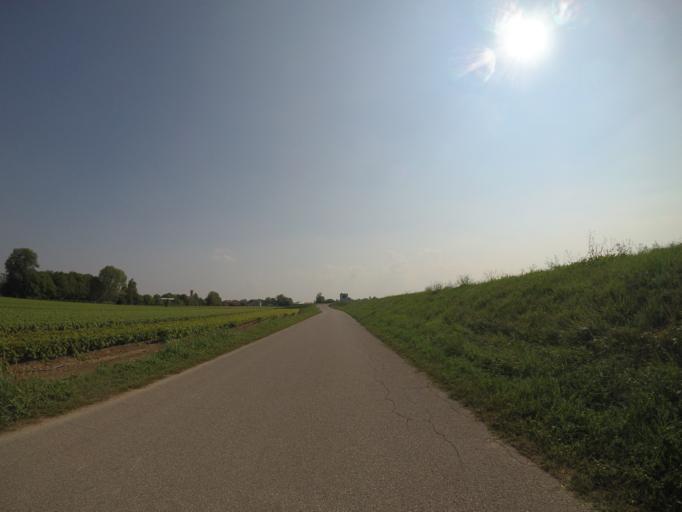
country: IT
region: Friuli Venezia Giulia
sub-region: Provincia di Udine
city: Camino al Tagliamento
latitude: 45.9201
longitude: 12.9258
